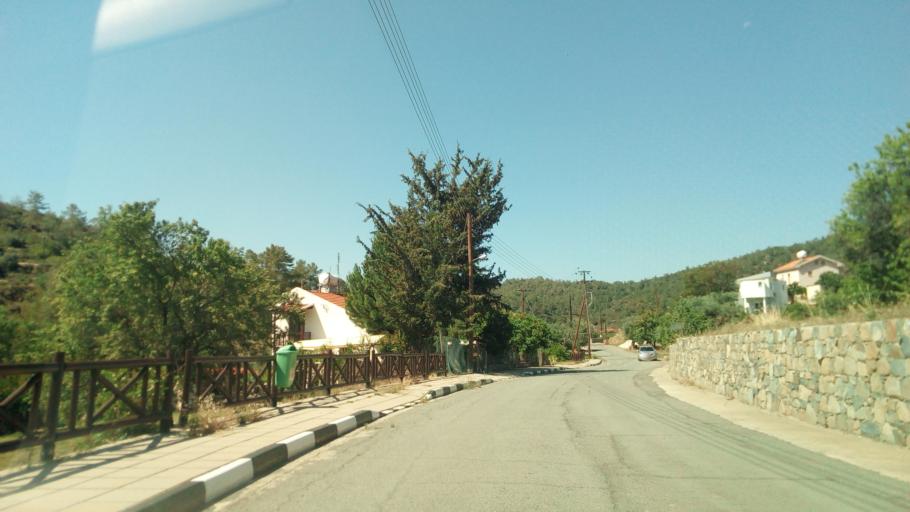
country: CY
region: Limassol
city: Parekklisha
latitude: 34.8662
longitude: 33.1559
